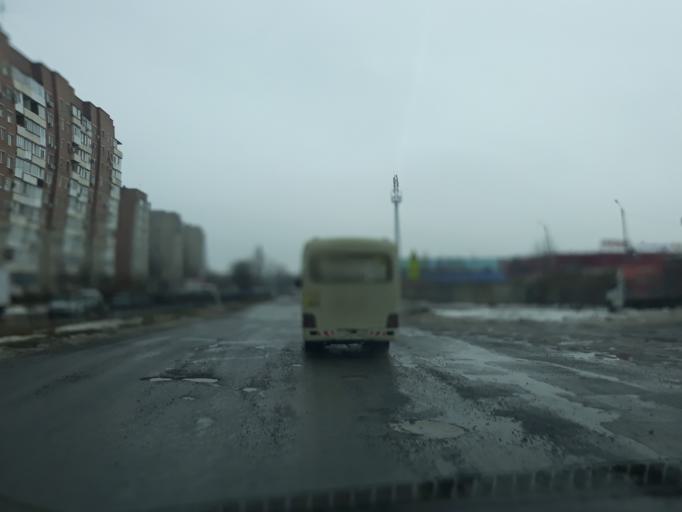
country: RU
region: Rostov
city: Novobessergenovka
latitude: 47.2189
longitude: 38.8615
